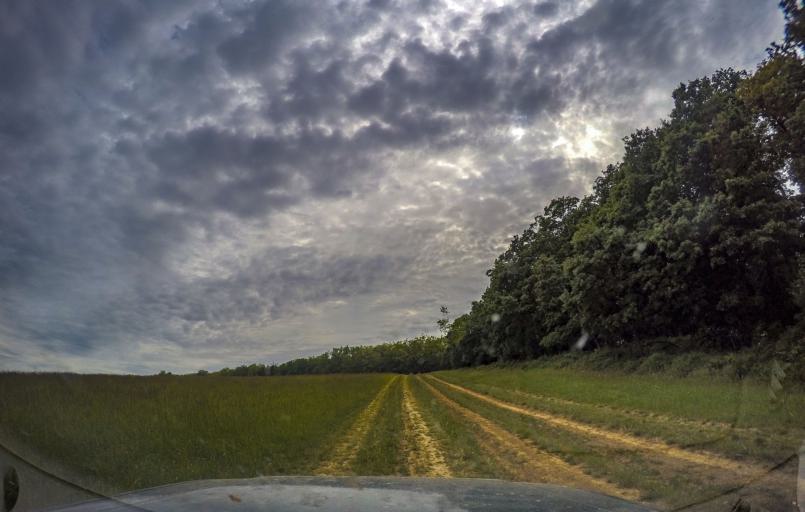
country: HU
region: Somogy
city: Karad
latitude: 46.7618
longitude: 17.8929
